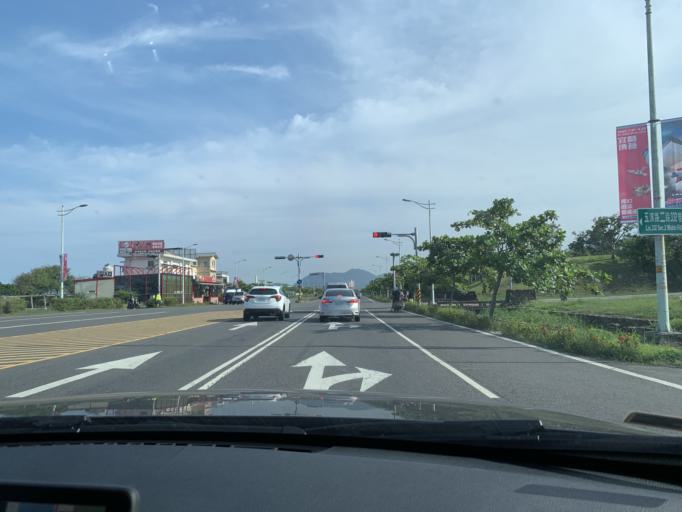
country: TW
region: Taiwan
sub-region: Yilan
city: Yilan
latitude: 24.6887
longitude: 121.8254
